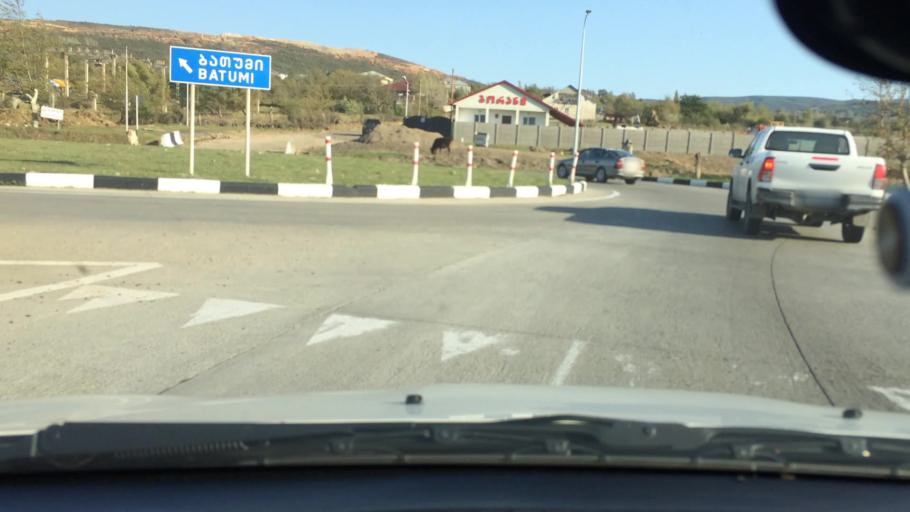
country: GE
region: Imereti
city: Kutaisi
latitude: 42.2133
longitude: 42.8193
